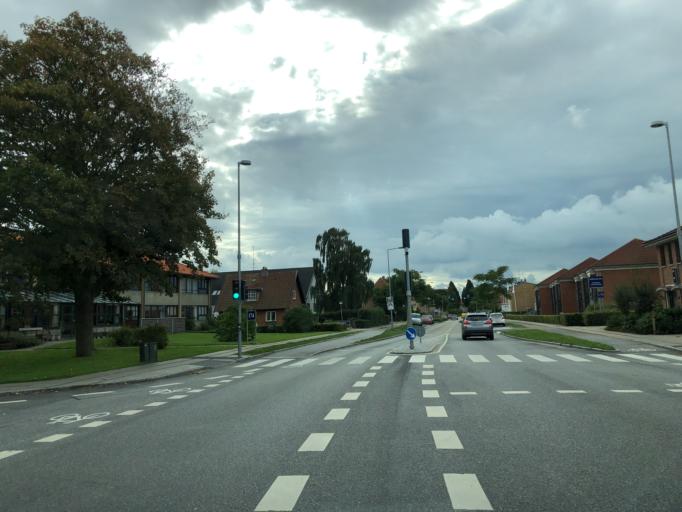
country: DK
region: South Denmark
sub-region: Sonderborg Kommune
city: Sonderborg
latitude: 54.9142
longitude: 9.8030
